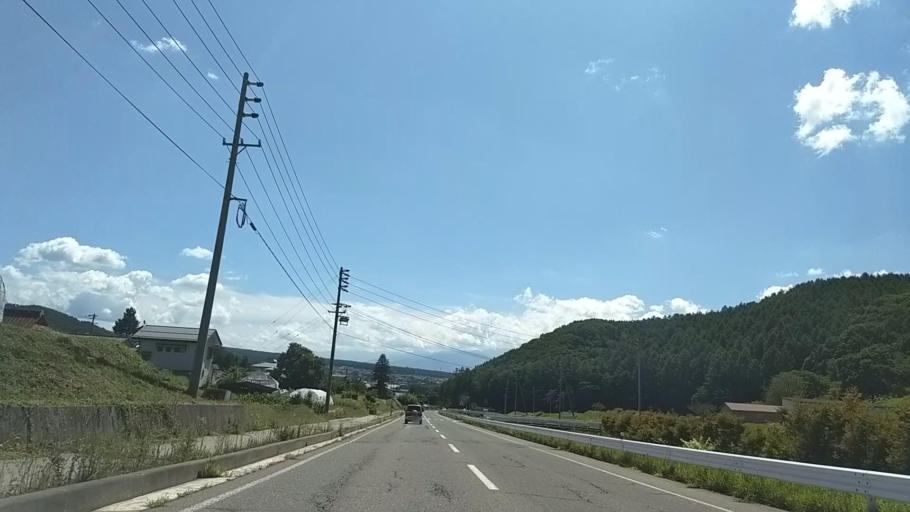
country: JP
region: Nagano
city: Chino
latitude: 36.0565
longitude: 138.2242
